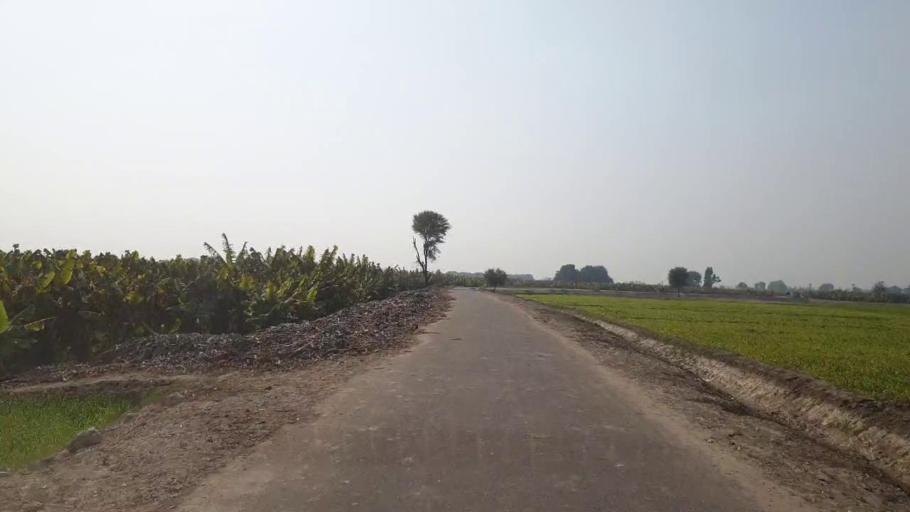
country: PK
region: Sindh
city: Bhit Shah
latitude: 25.7856
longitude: 68.4901
